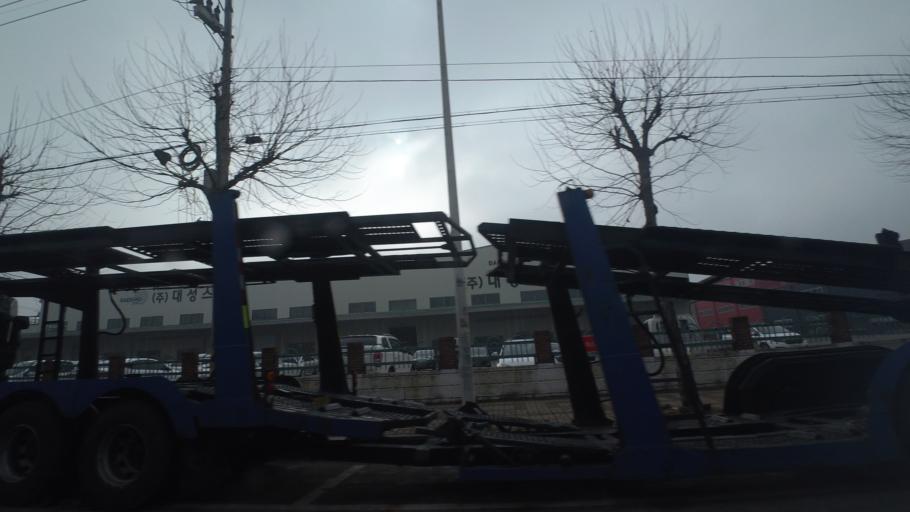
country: KR
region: Gyeonggi-do
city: Hwaseong-si
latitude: 36.9880
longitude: 126.8521
